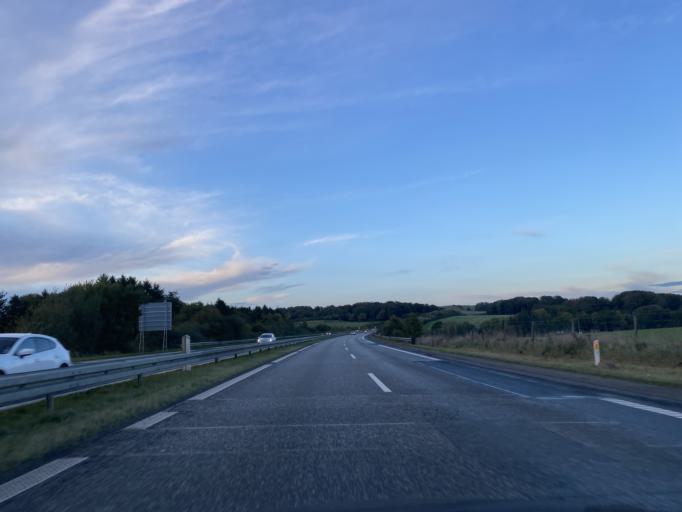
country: DK
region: Central Jutland
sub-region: Horsens Kommune
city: Horsens
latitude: 55.9395
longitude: 9.8192
